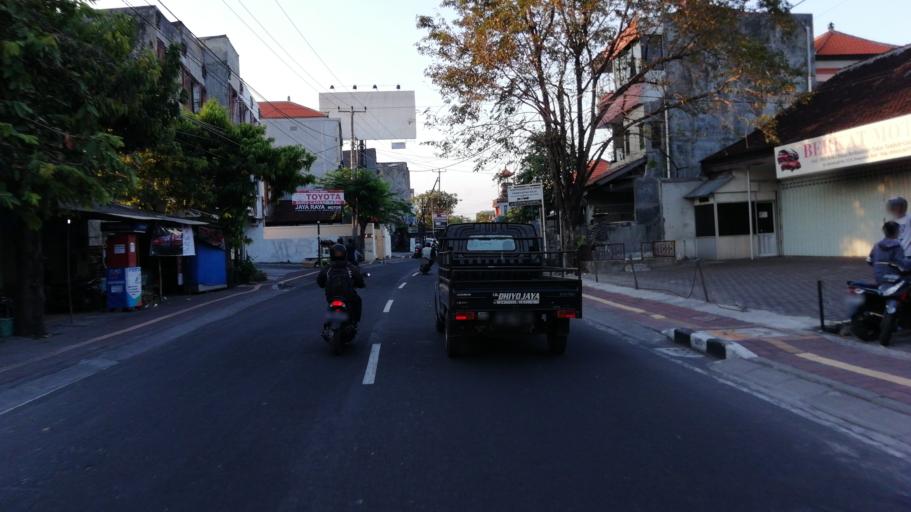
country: ID
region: Bali
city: Denpasar
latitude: -8.6489
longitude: 115.2090
